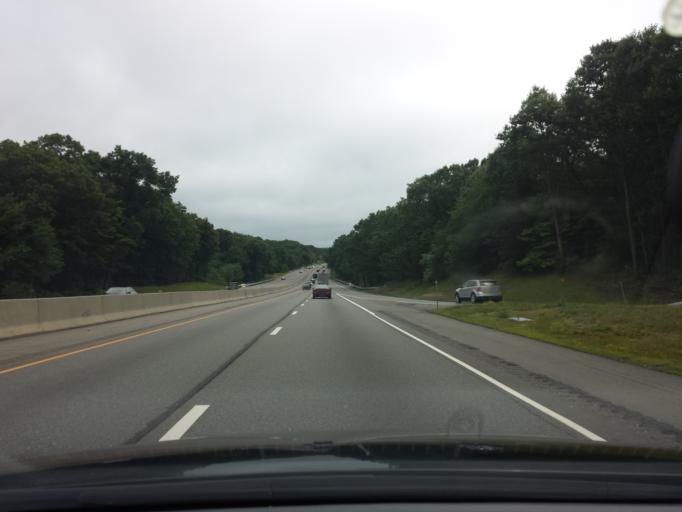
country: US
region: Connecticut
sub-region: Middlesex County
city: Clinton
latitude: 41.2883
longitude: -72.5271
